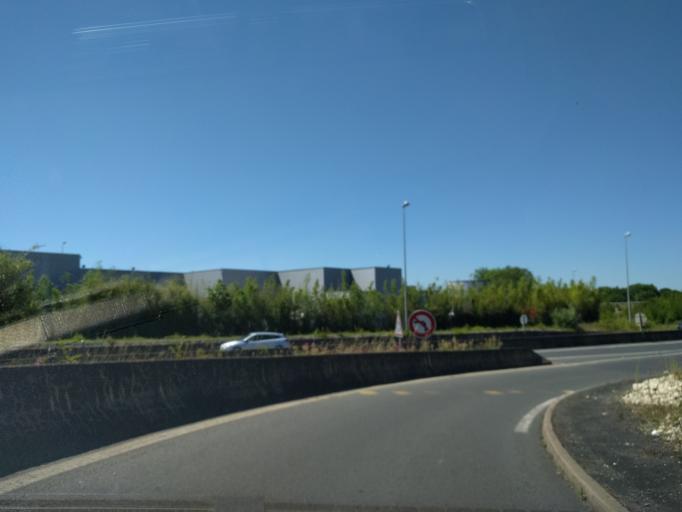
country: FR
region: Poitou-Charentes
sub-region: Departement des Deux-Sevres
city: Chauray
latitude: 46.3379
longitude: -0.4081
